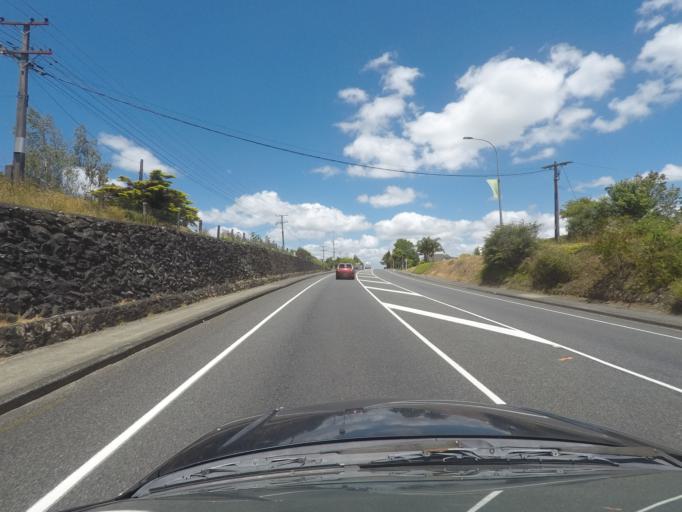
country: NZ
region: Northland
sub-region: Whangarei
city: Whangarei
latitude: -35.7464
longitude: 174.3676
